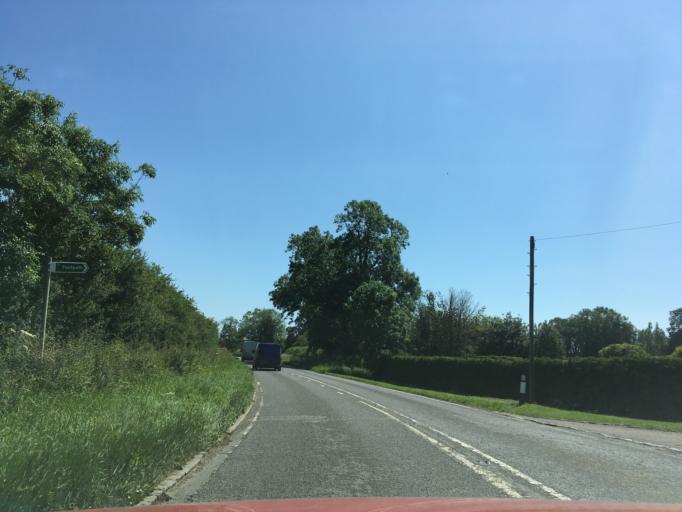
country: GB
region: England
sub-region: Northamptonshire
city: Brackley
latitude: 51.9962
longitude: -1.1786
